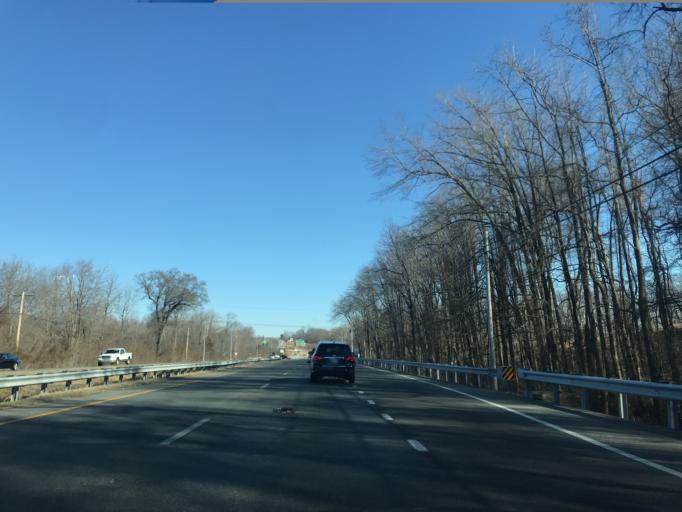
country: US
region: Maryland
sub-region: Prince George's County
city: Accokeek
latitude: 38.6522
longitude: -76.9815
